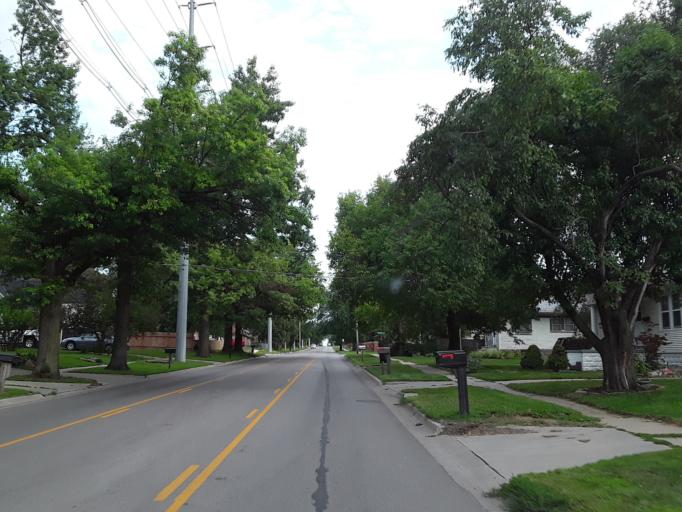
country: US
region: Nebraska
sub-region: Lancaster County
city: Lincoln
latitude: 40.8413
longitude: -96.6442
